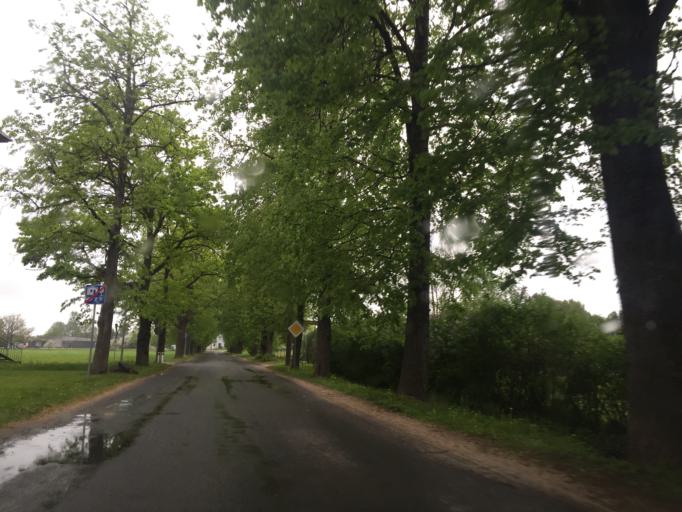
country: LV
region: Lielvarde
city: Lielvarde
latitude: 56.7136
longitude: 24.8327
